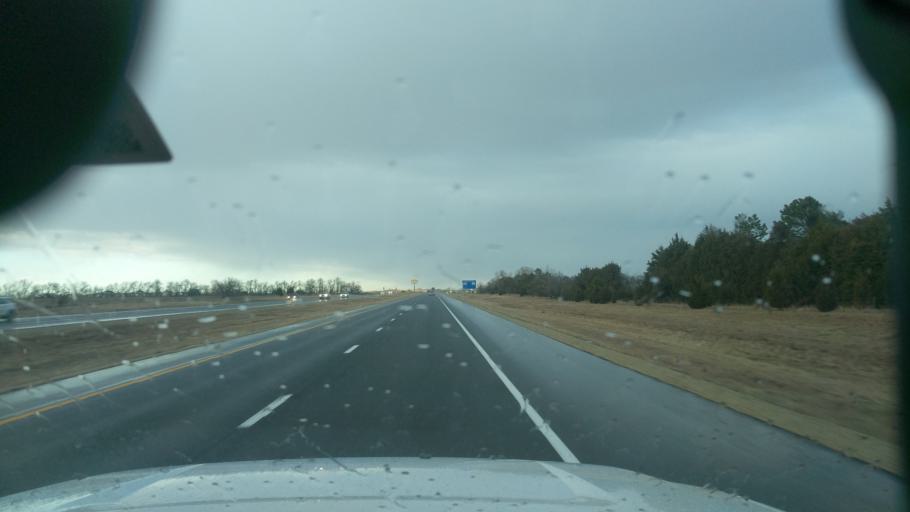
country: US
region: Kansas
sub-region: Harvey County
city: Newton
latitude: 37.9872
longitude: -97.3273
